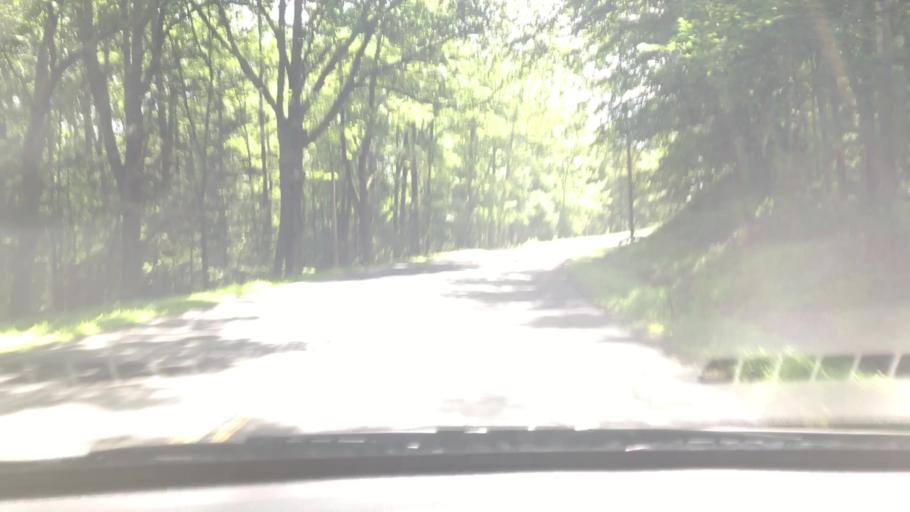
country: US
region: New York
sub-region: Ulster County
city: Shokan
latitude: 41.9504
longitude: -74.2445
